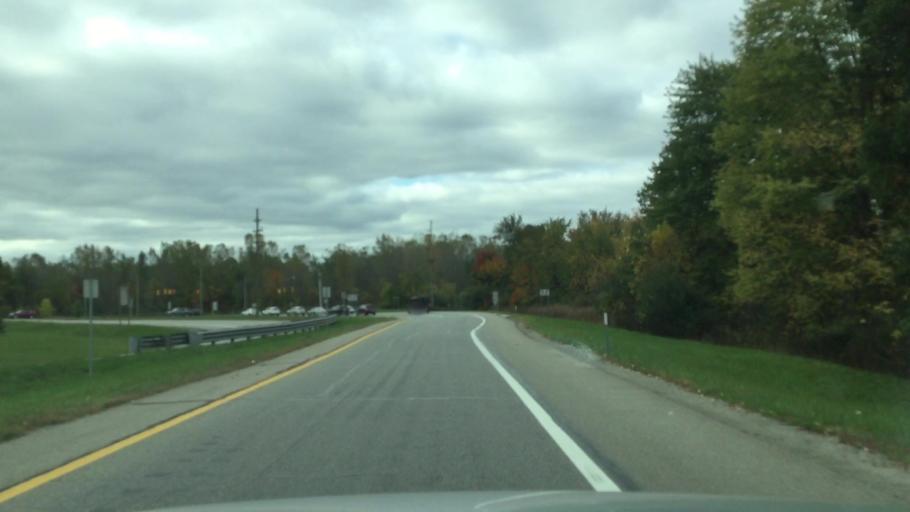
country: US
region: Michigan
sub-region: Macomb County
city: Shelby
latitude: 42.6714
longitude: -83.0165
